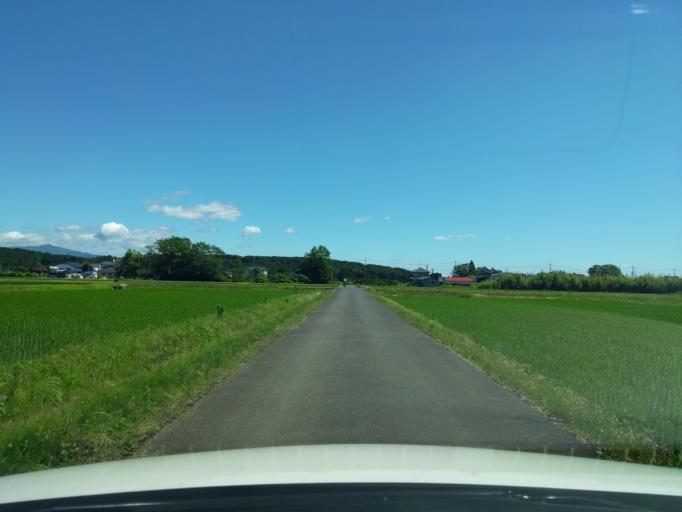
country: JP
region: Fukushima
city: Koriyama
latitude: 37.3861
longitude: 140.3037
